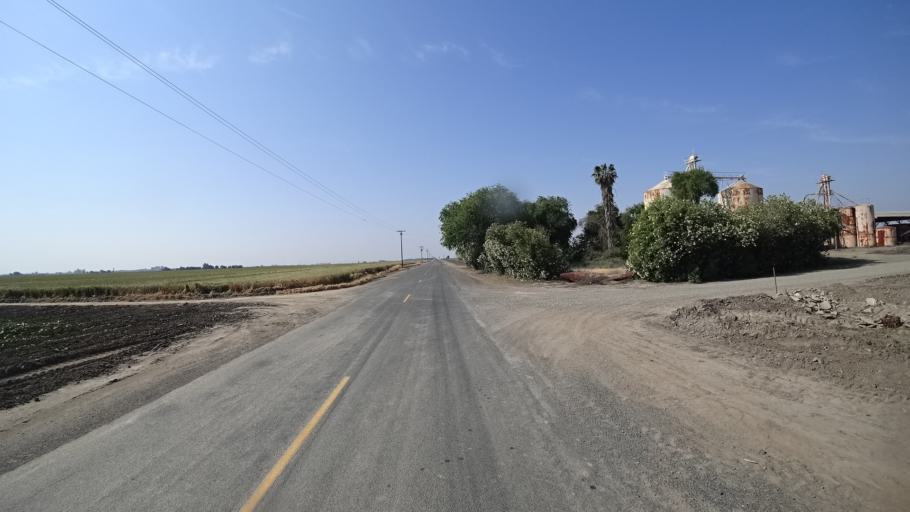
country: US
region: California
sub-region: Kings County
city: Lemoore
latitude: 36.3245
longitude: -119.8437
